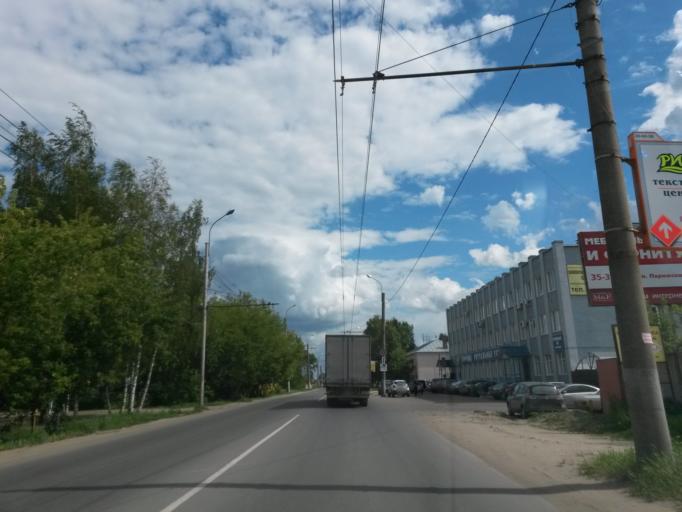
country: RU
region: Ivanovo
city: Novo-Talitsy
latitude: 57.0002
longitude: 40.9016
